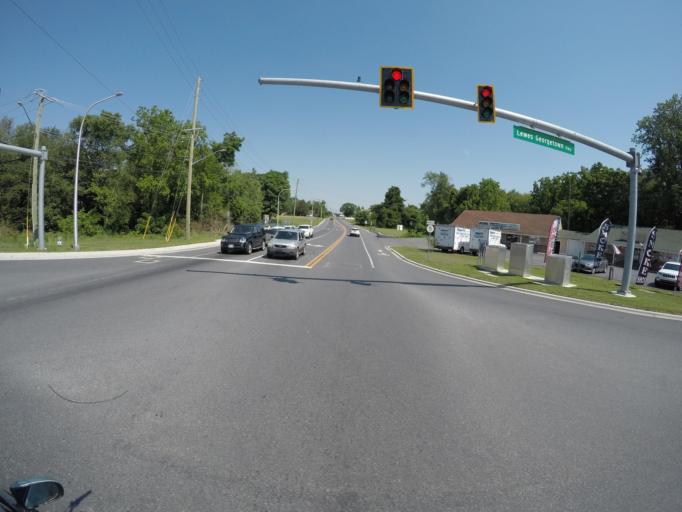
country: US
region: Delaware
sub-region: Sussex County
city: Milton
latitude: 38.7252
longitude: -75.2856
